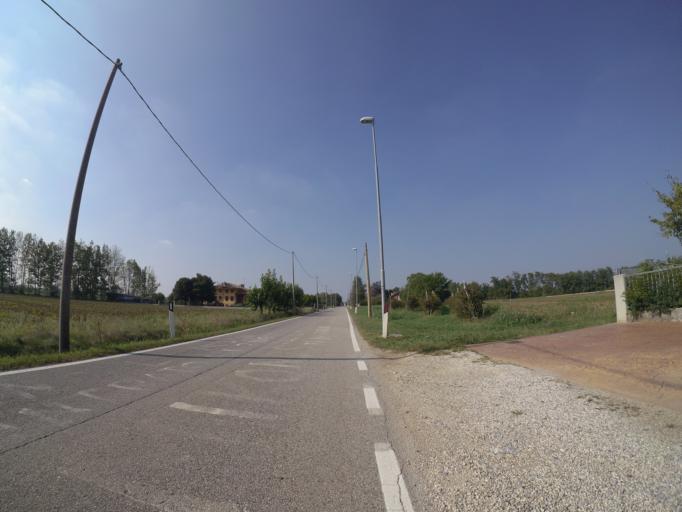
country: IT
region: Friuli Venezia Giulia
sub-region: Provincia di Udine
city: Basiliano
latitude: 45.9872
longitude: 13.0324
